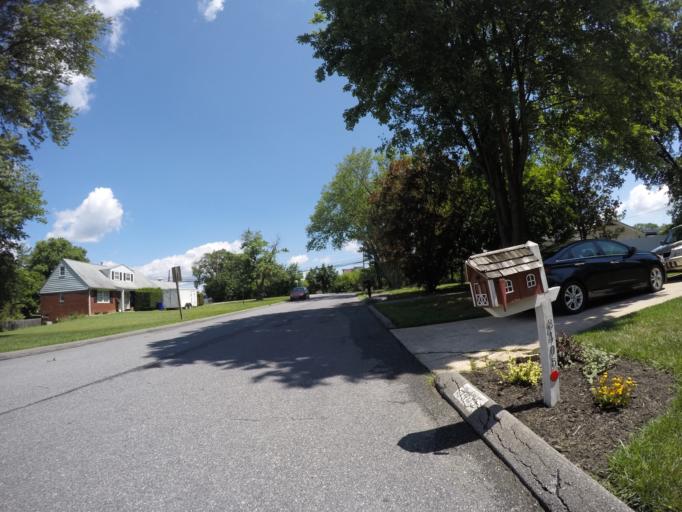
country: US
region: Maryland
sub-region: Howard County
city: Columbia
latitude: 39.2768
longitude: -76.8598
